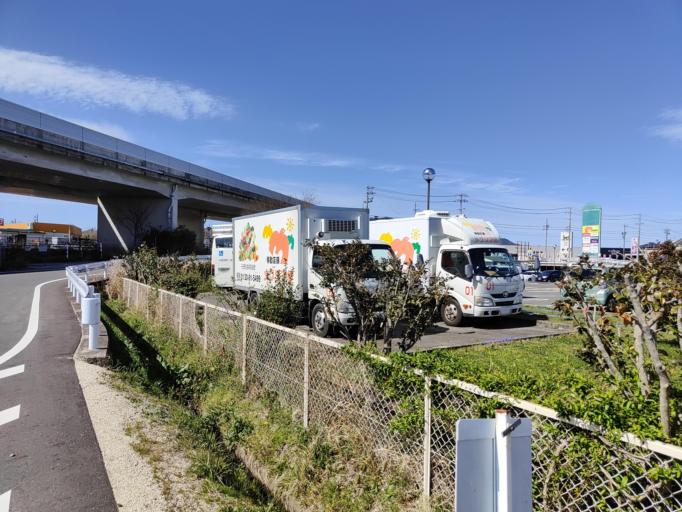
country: JP
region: Aichi
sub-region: Toyota-shi
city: Toyota
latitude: 35.1506
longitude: 137.1795
